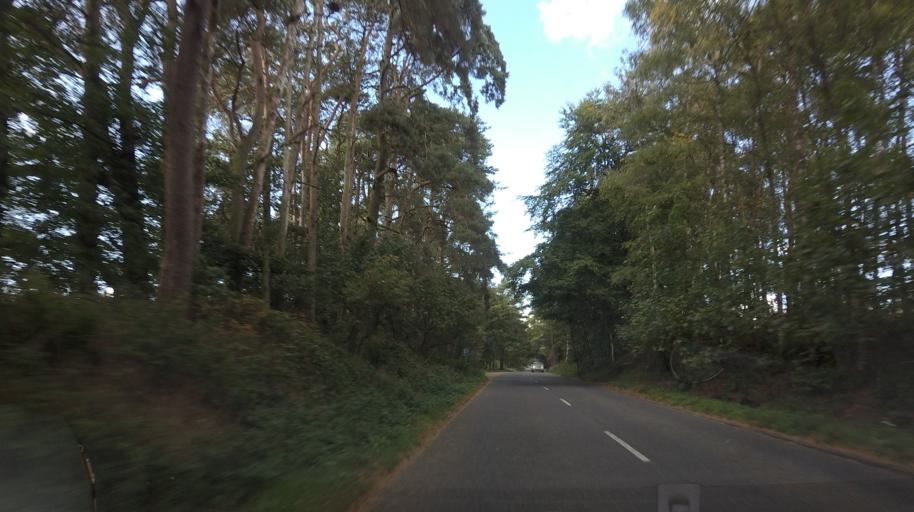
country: GB
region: Scotland
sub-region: Aberdeenshire
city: Banchory
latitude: 57.1129
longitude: -2.4256
